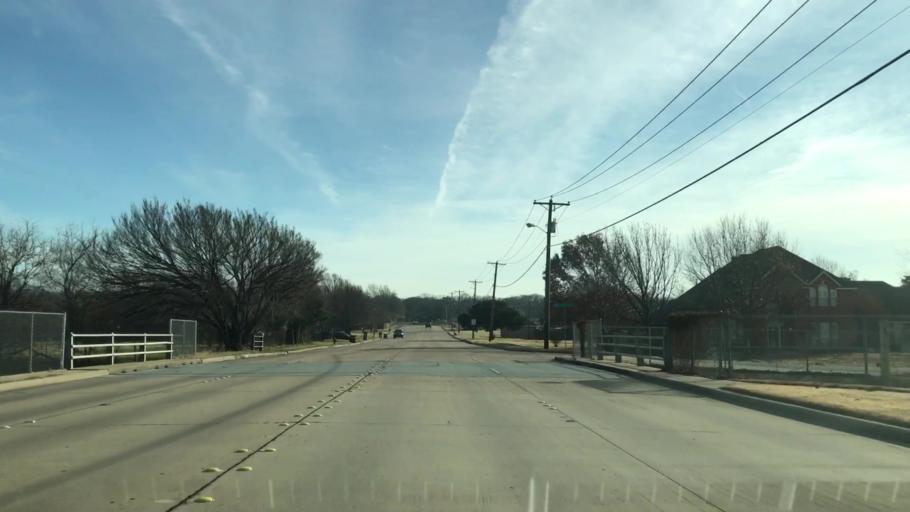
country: US
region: Texas
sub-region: Tarrant County
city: Watauga
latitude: 32.8749
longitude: -97.2232
